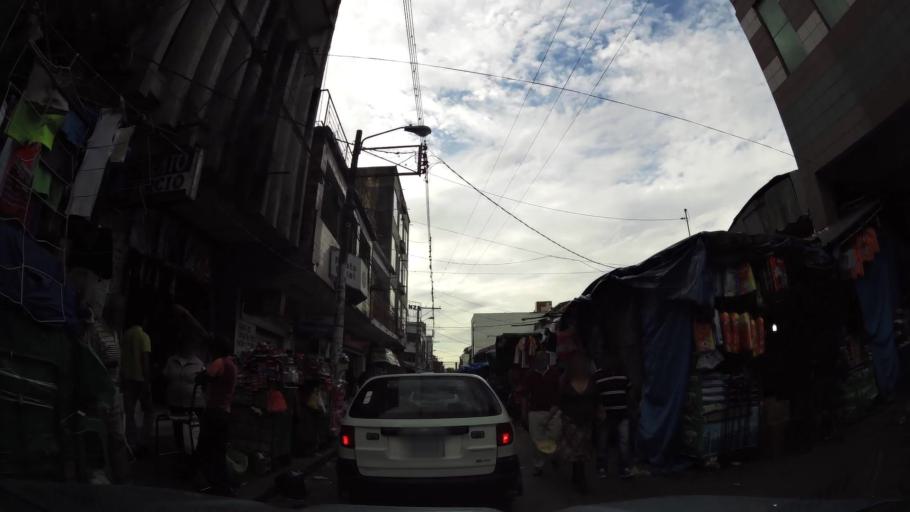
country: BO
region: Santa Cruz
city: Santa Cruz de la Sierra
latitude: -17.7784
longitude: -63.1780
